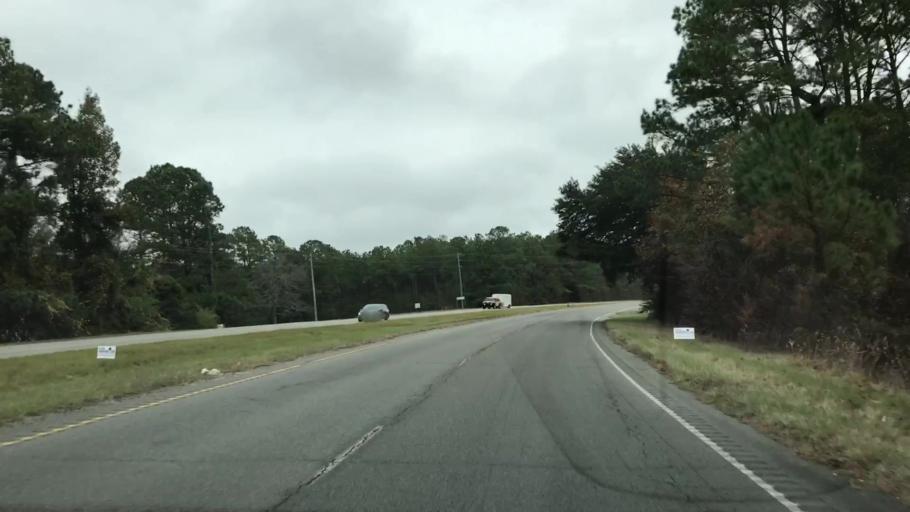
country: US
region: South Carolina
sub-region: Charleston County
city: Awendaw
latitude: 33.0373
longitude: -79.6164
